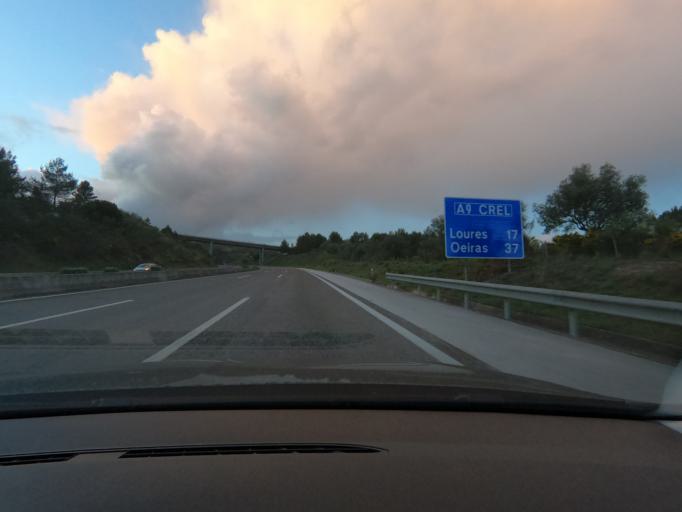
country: PT
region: Lisbon
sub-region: Vila Franca de Xira
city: Vialonga
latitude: 38.9007
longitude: -9.0559
